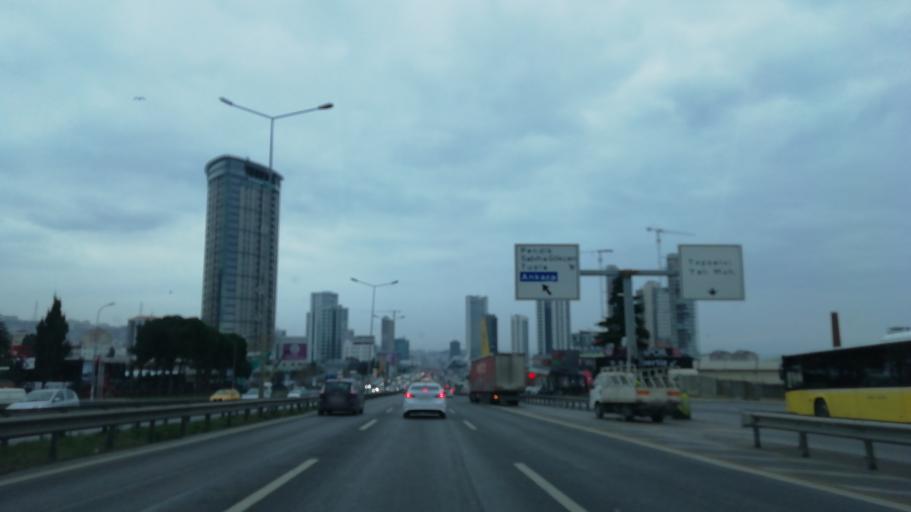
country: TR
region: Istanbul
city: Pendik
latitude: 40.9045
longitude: 29.2136
